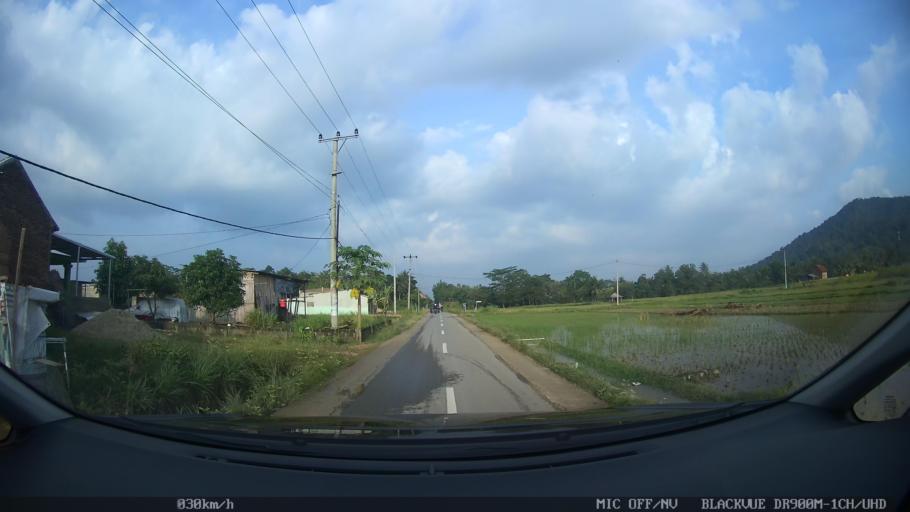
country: ID
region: Lampung
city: Kedaton
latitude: -5.3921
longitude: 105.3274
